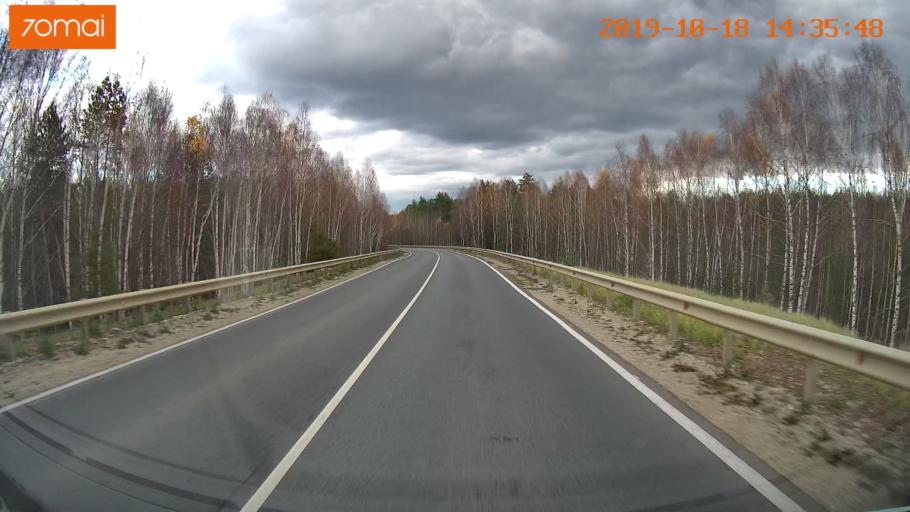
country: RU
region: Vladimir
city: Velikodvorskiy
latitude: 55.2216
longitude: 40.6463
